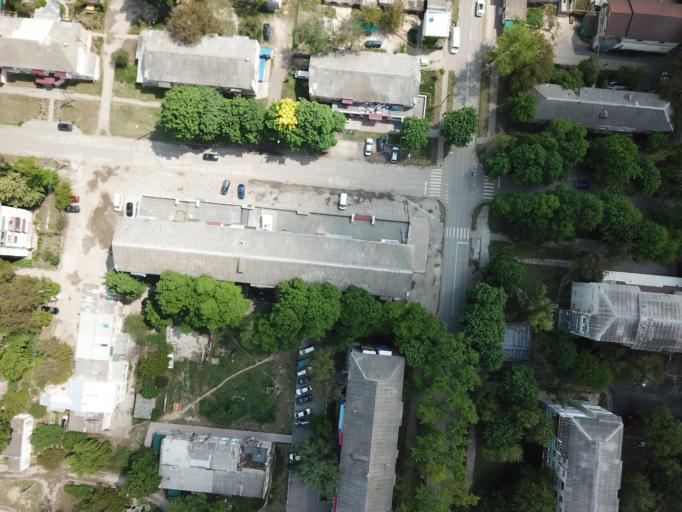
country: MD
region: Ungheni
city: Ungheni
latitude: 47.2167
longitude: 27.8000
